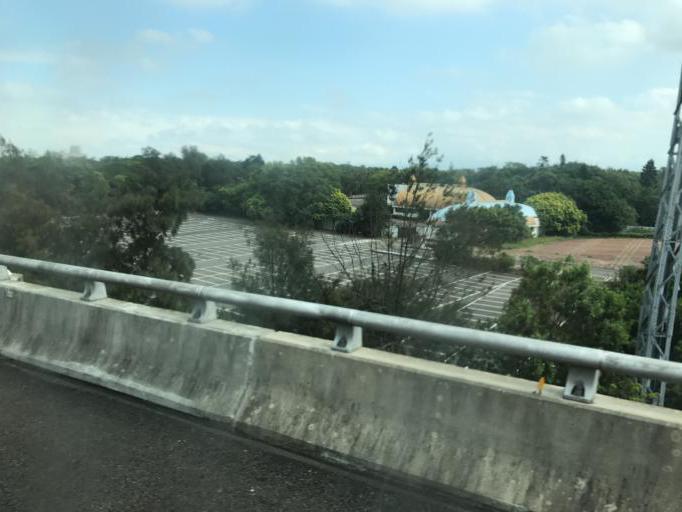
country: TW
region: Taiwan
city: Daxi
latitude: 24.9274
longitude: 121.1743
